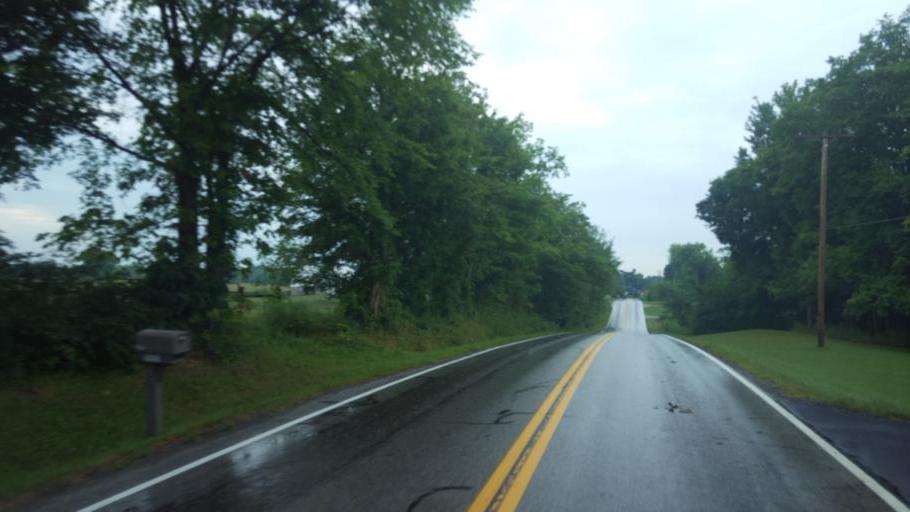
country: US
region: Ohio
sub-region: Geauga County
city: Middlefield
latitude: 41.4163
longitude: -81.0148
